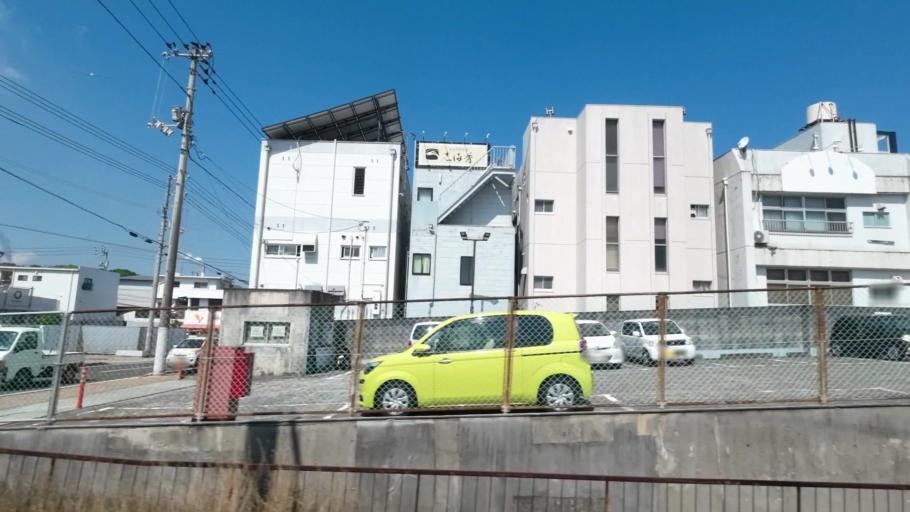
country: JP
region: Ehime
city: Kawanoecho
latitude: 34.0114
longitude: 133.5754
